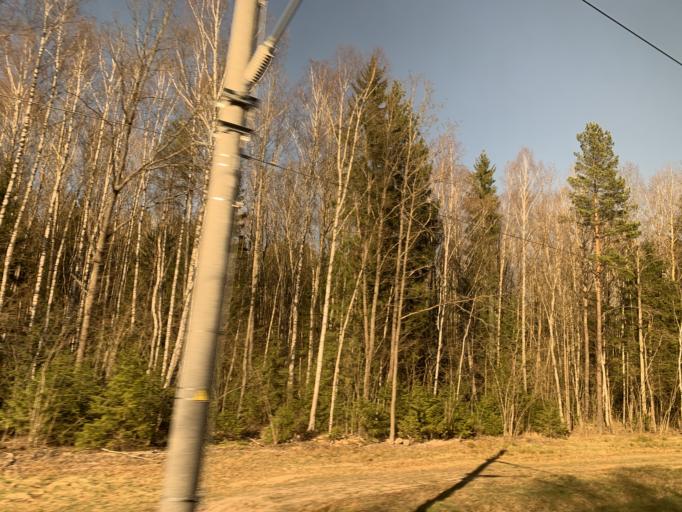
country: BY
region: Grodnenskaya
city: Smarhon'
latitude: 54.4867
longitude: 26.3136
